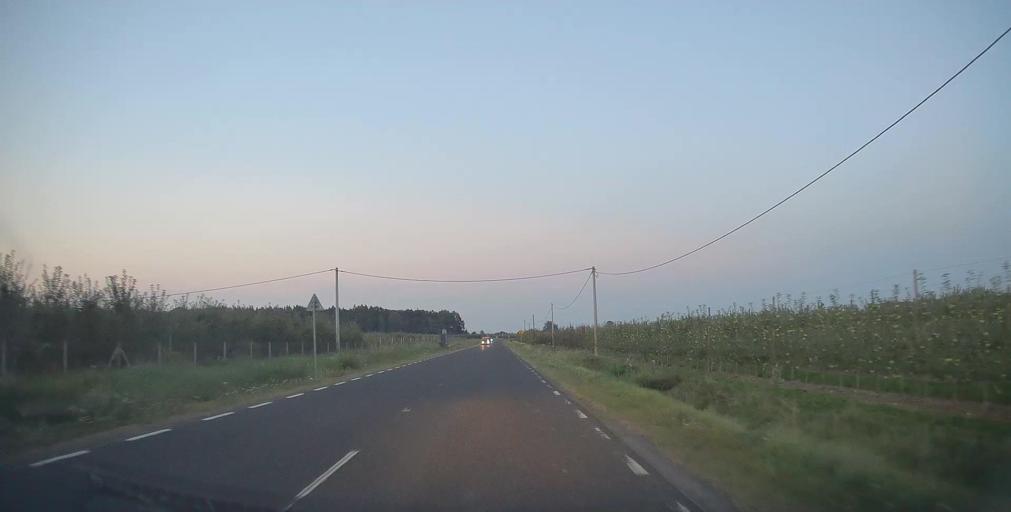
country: PL
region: Masovian Voivodeship
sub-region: Powiat grojecki
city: Grojec
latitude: 51.8288
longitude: 20.8820
